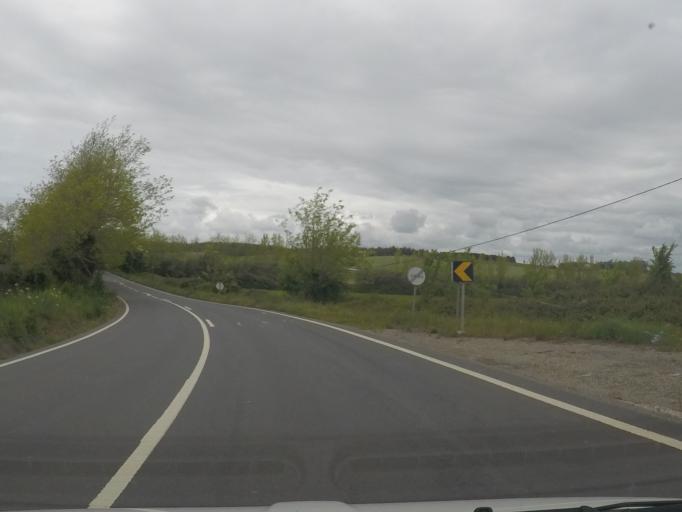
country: PT
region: Setubal
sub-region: Santiago do Cacem
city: Cercal
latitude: 37.8188
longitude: -8.6833
